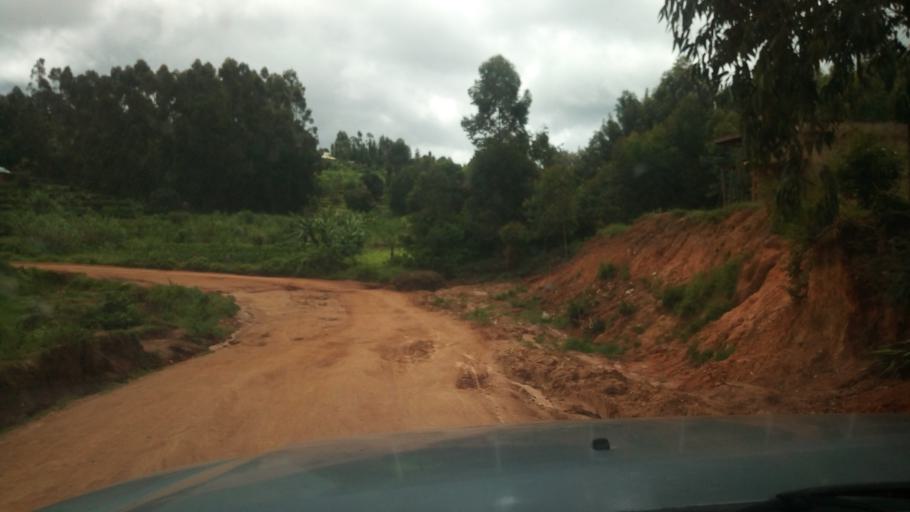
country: KE
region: Makueni
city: Wote
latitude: -1.6679
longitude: 37.4497
